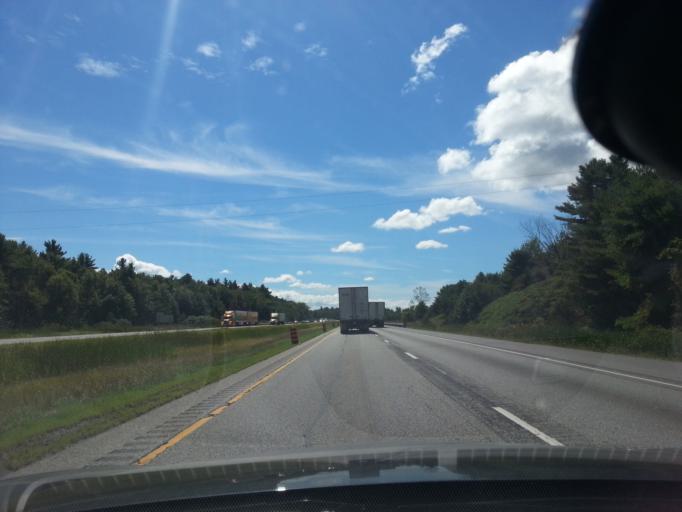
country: US
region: New York
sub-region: Jefferson County
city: Alexandria Bay
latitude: 44.4581
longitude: -75.8829
